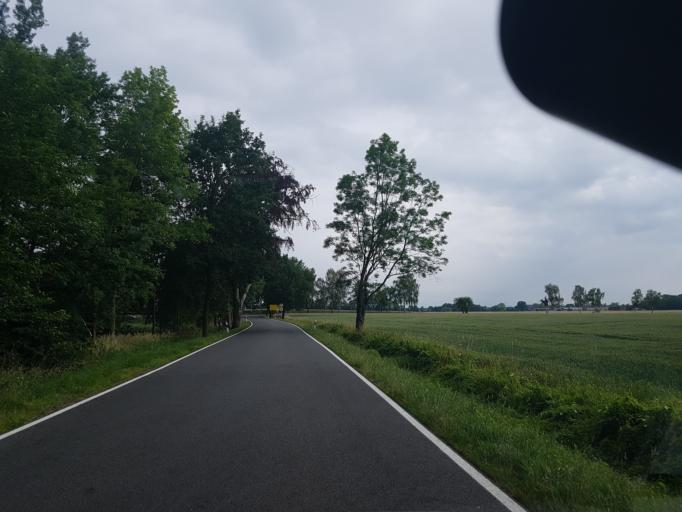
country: DE
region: Brandenburg
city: Sonnewalde
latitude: 51.6993
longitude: 13.6219
